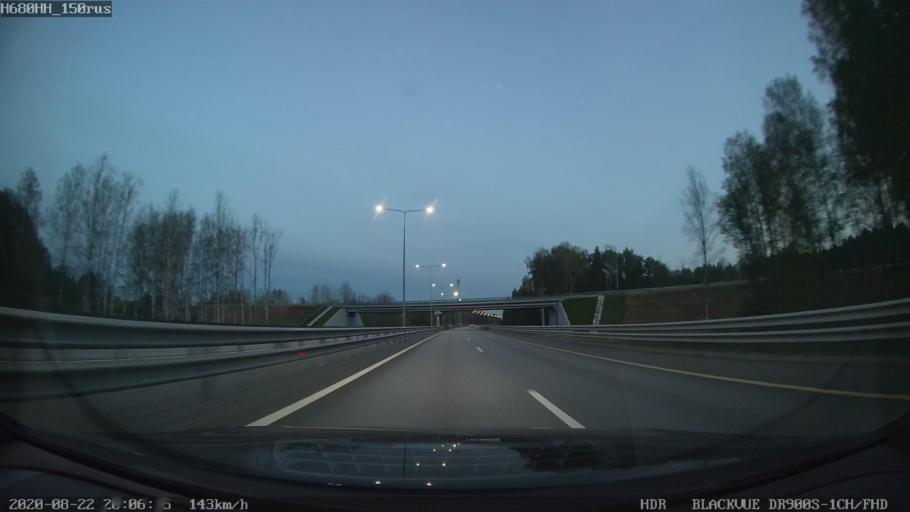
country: RU
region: Tverskaya
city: Novozavidovskiy
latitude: 56.6190
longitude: 36.4442
